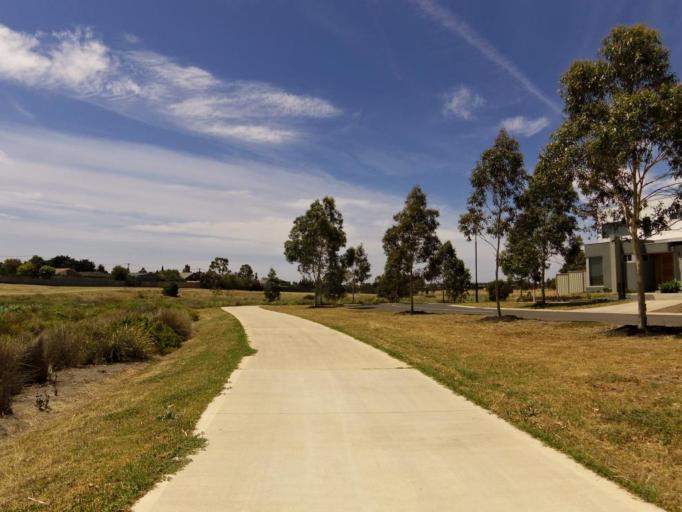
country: AU
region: Victoria
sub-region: Wyndham
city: Williams Landing
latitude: -37.8650
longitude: 144.7187
